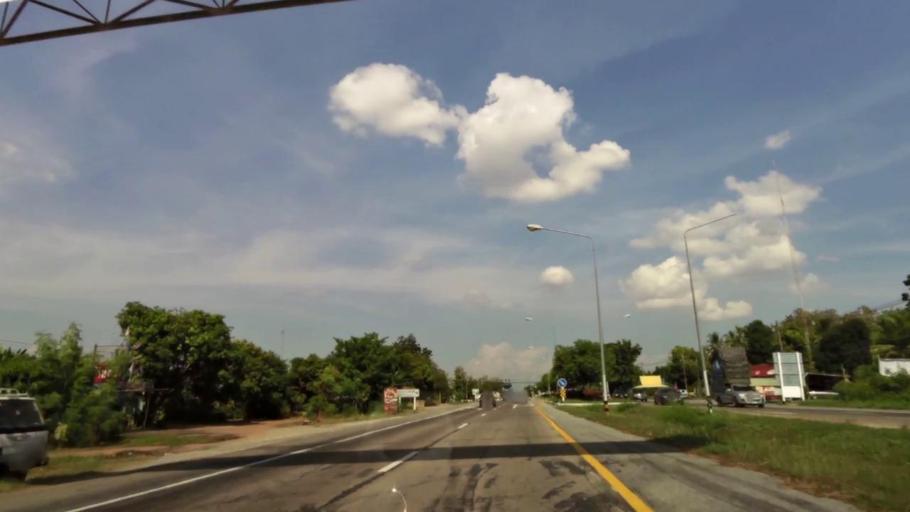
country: TH
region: Uttaradit
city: Thong Saen Khan
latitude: 17.4698
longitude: 100.2364
